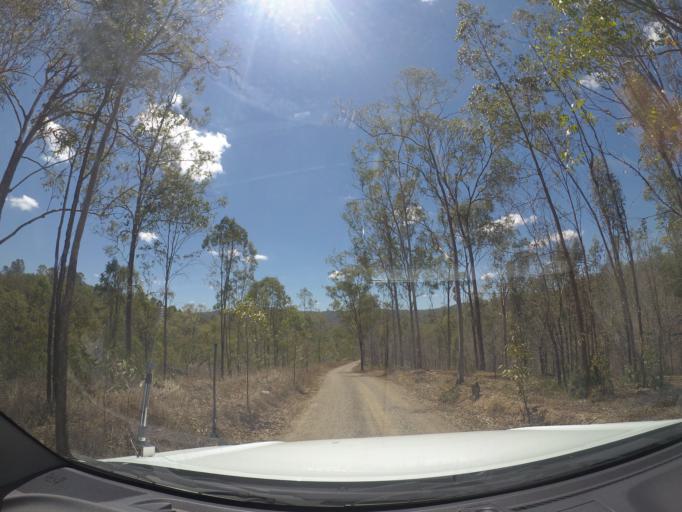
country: AU
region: Queensland
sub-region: Ipswich
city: Springfield Lakes
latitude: -27.8208
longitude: 152.8443
